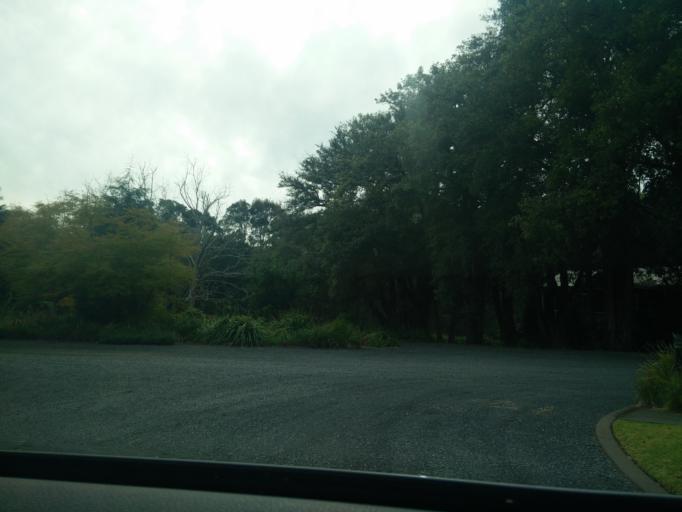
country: AU
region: New South Wales
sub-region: Gosford Shire
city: Bensville
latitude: -33.5194
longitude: 151.3746
